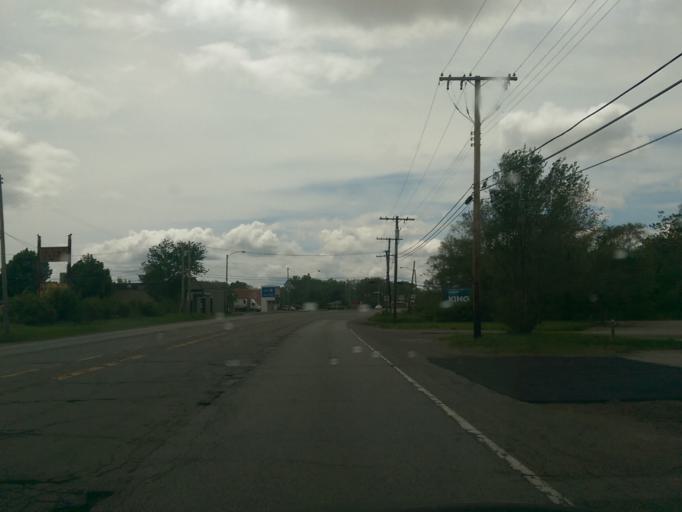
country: US
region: Indiana
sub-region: Lake County
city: Lake Station
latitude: 41.5968
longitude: -87.2635
